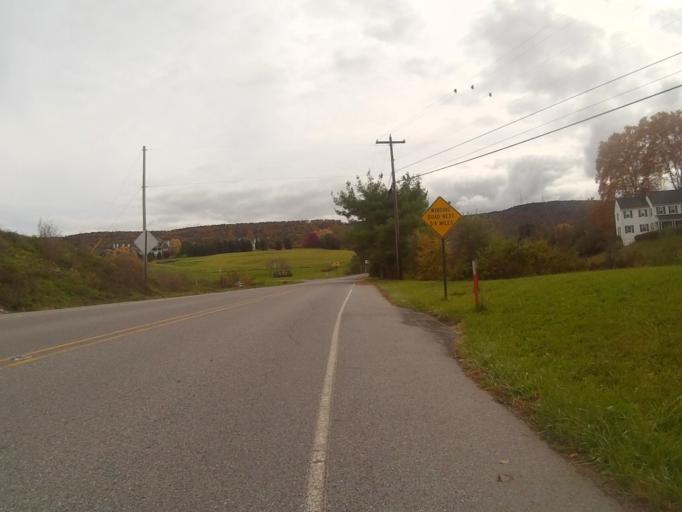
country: US
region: Pennsylvania
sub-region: Centre County
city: Boalsburg
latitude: 40.7782
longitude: -77.7583
